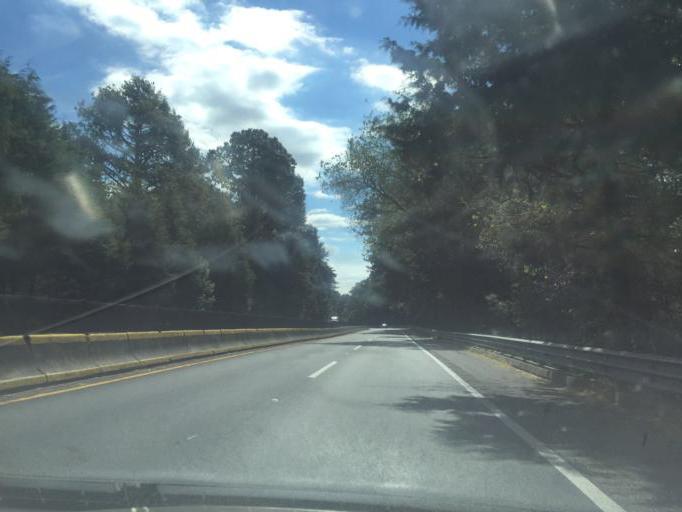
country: MX
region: Morelos
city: Tres Marias
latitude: 19.0417
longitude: -99.2320
